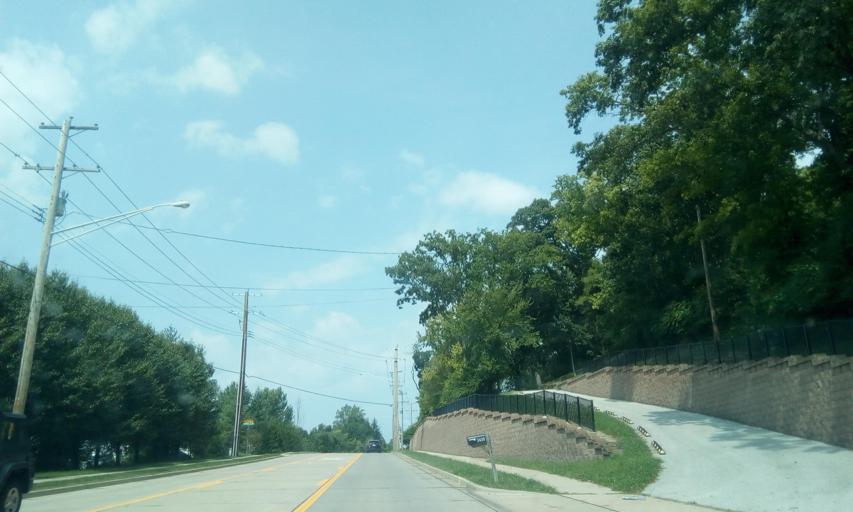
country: US
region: Missouri
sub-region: Saint Louis County
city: Town and Country
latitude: 38.5886
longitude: -90.4696
